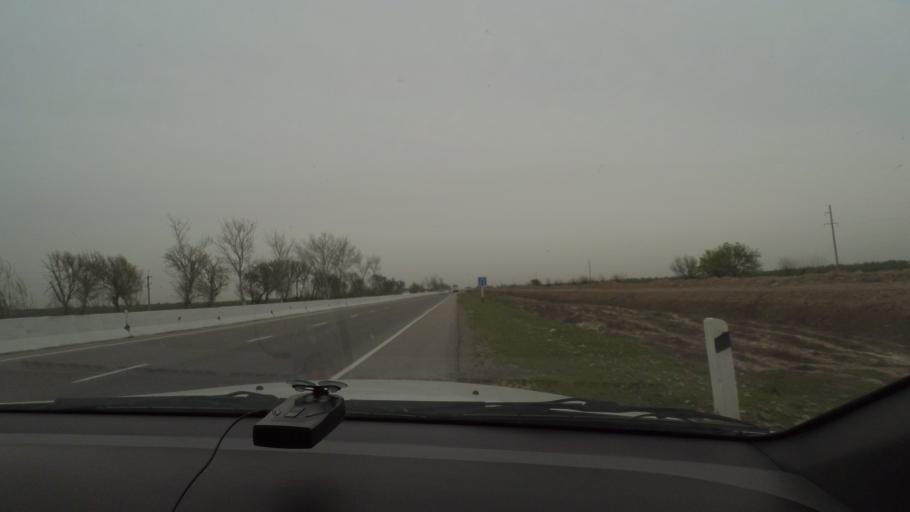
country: UZ
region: Jizzax
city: Dustlik
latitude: 40.4023
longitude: 68.1918
